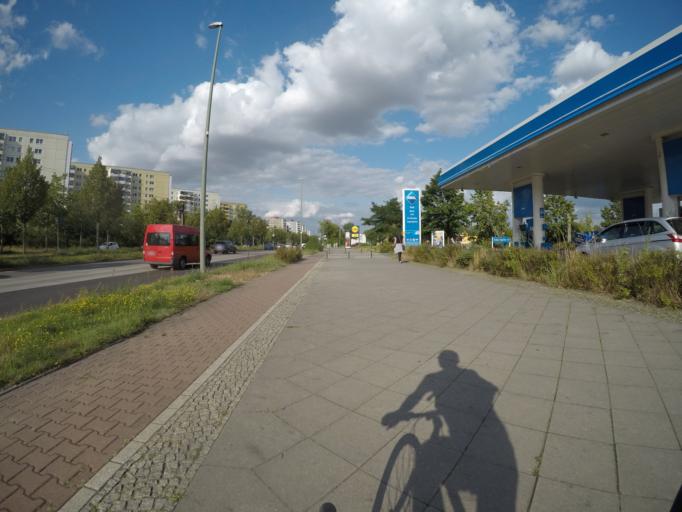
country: DE
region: Berlin
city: Marzahn
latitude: 52.5465
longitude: 13.5740
